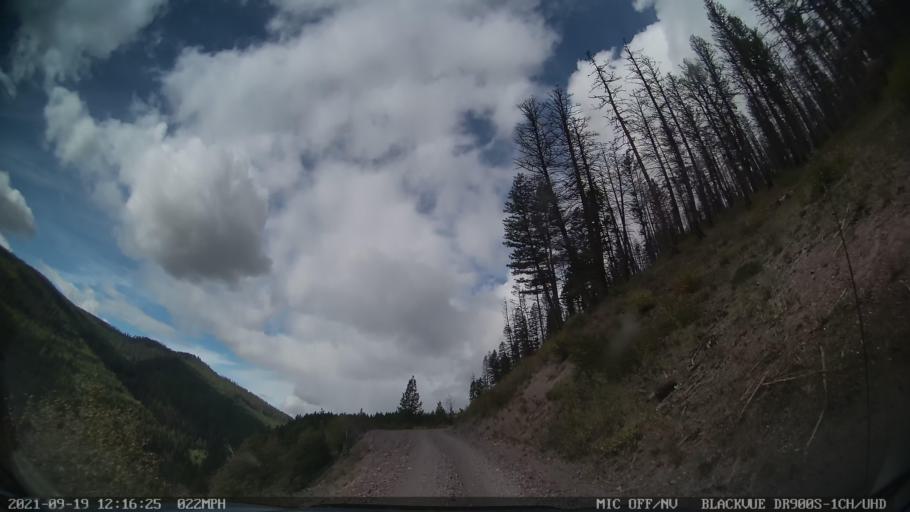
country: US
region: Montana
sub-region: Missoula County
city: Seeley Lake
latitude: 47.1694
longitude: -113.3513
